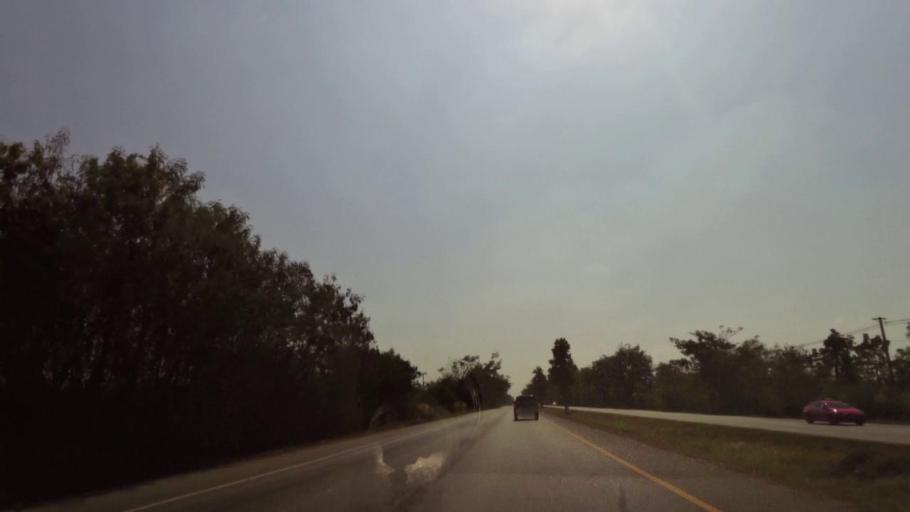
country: TH
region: Phichit
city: Bueng Na Rang
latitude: 16.3323
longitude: 100.1284
